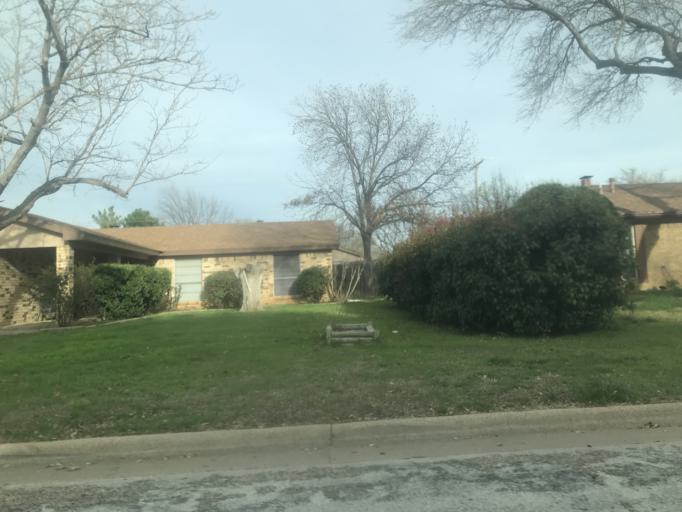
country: US
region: Texas
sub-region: Taylor County
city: Abilene
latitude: 32.3926
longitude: -99.7705
